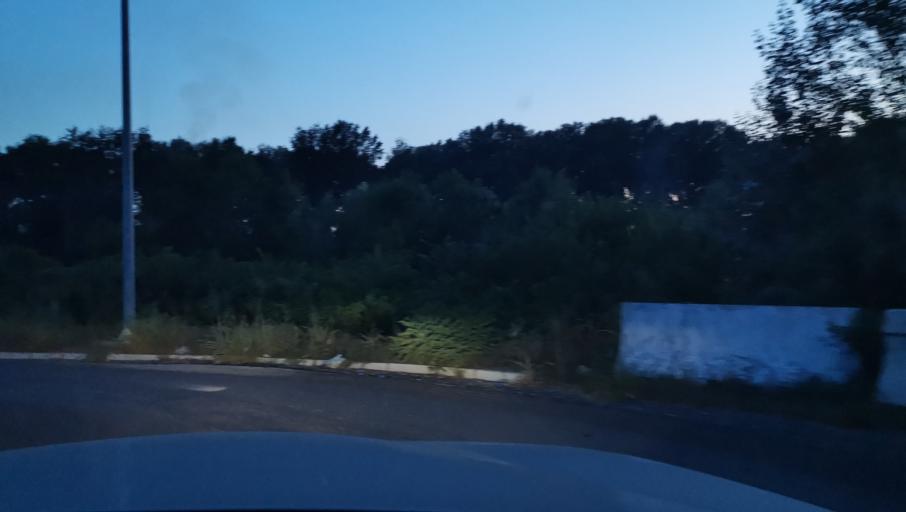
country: RS
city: Zvecka
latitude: 44.6788
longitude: 20.1674
